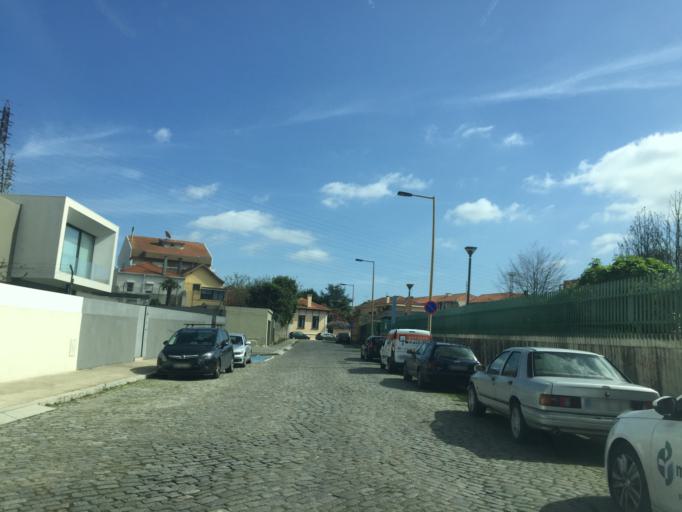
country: PT
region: Porto
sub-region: Matosinhos
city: Senhora da Hora
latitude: 41.1762
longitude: -8.6581
